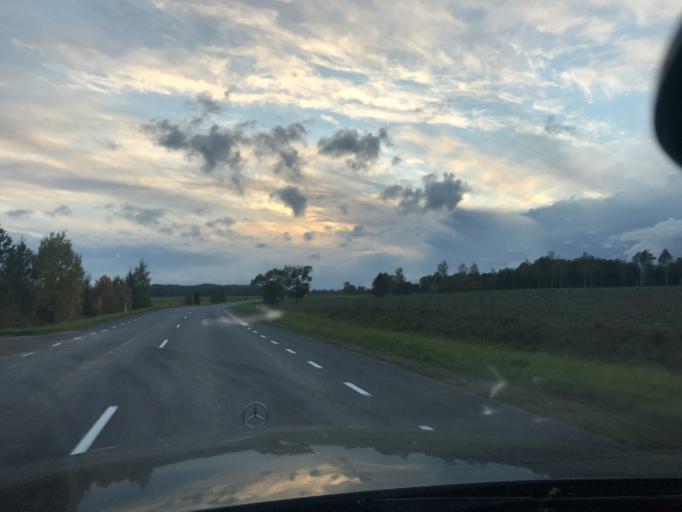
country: EE
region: Valgamaa
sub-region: Torva linn
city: Torva
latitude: 57.9788
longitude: 25.9924
